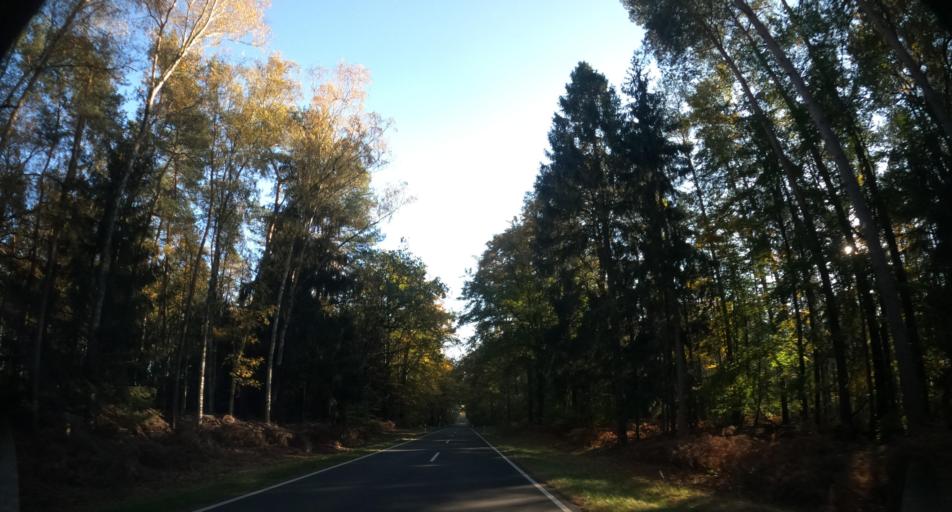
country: DE
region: Mecklenburg-Vorpommern
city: Ahlbeck
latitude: 53.6581
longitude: 14.1843
